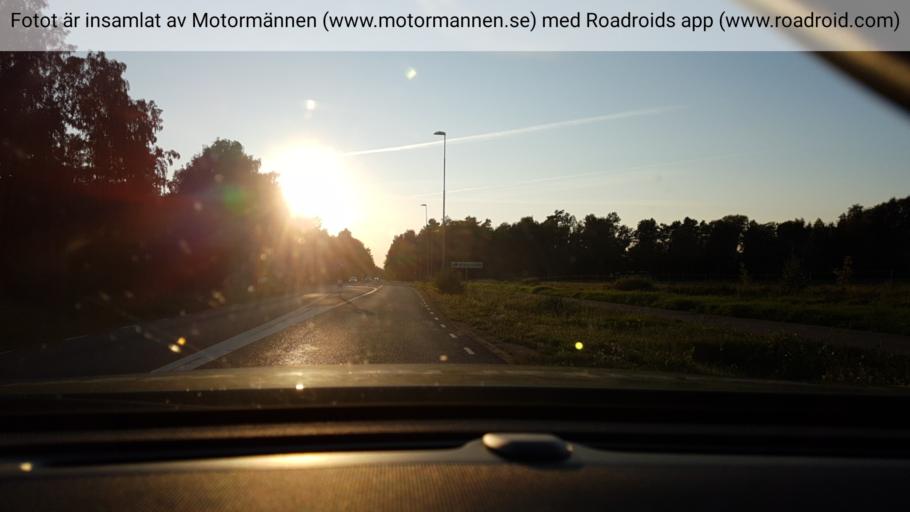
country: SE
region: Halland
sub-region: Halmstads Kommun
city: Mjallby
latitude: 56.6548
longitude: 12.7774
